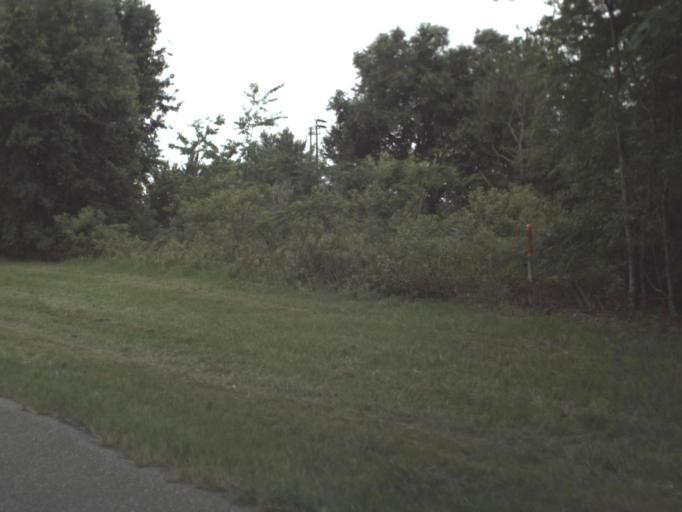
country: US
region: Florida
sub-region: Alachua County
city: Newberry
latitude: 29.6222
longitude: -82.5988
